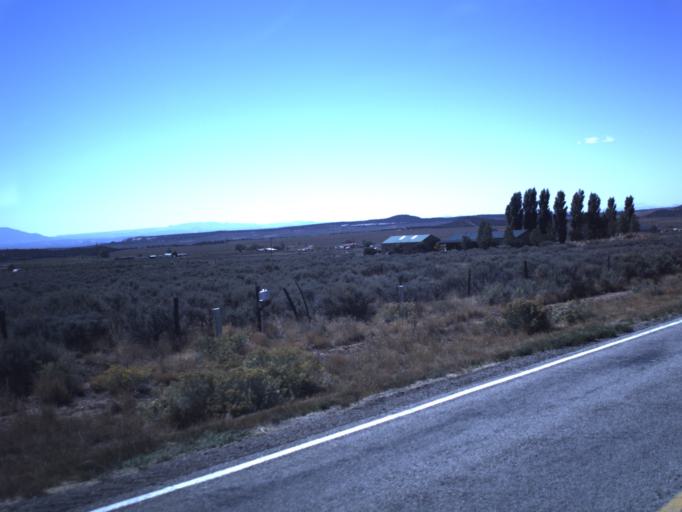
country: US
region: Utah
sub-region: Grand County
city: Moab
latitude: 38.3095
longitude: -109.2841
